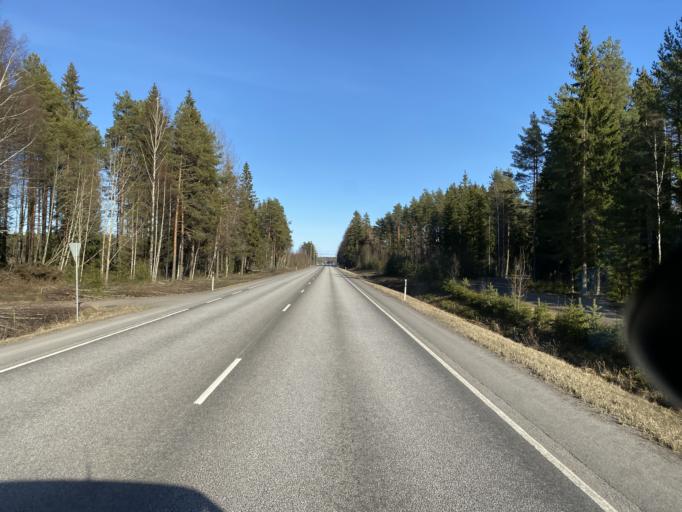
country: FI
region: Satakunta
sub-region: Rauma
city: Eura
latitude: 61.1313
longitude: 22.1031
